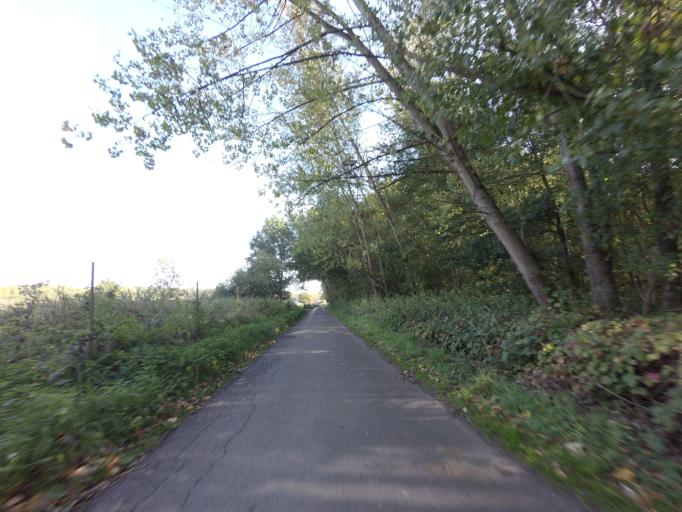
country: BE
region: Flanders
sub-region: Provincie Vlaams-Brabant
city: Kampenhout
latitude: 50.9226
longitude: 4.5941
